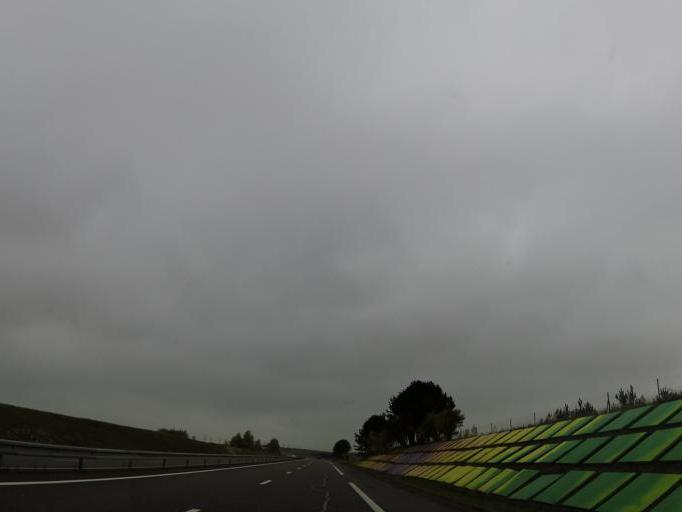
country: FR
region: Champagne-Ardenne
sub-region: Departement de la Marne
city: Courtisols
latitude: 49.0296
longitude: 4.5404
